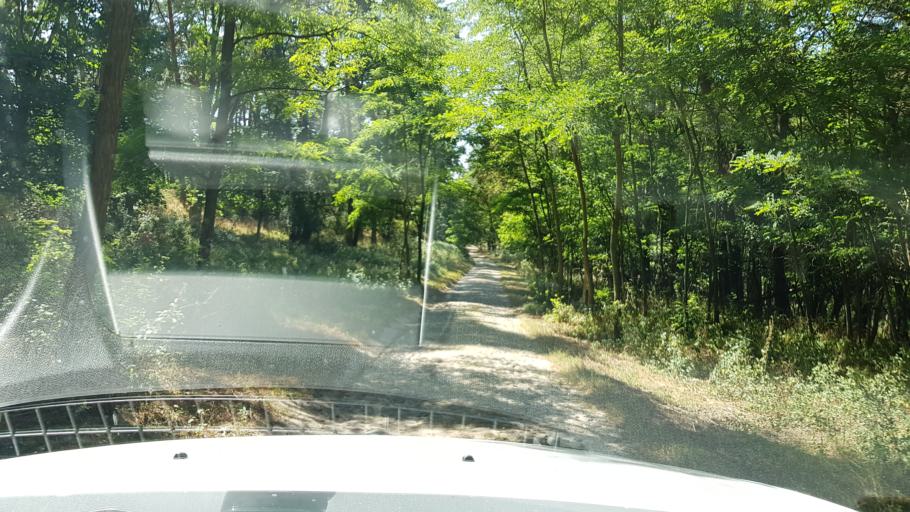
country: PL
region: West Pomeranian Voivodeship
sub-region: Powiat gryfinski
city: Cedynia
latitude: 52.8499
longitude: 14.2454
